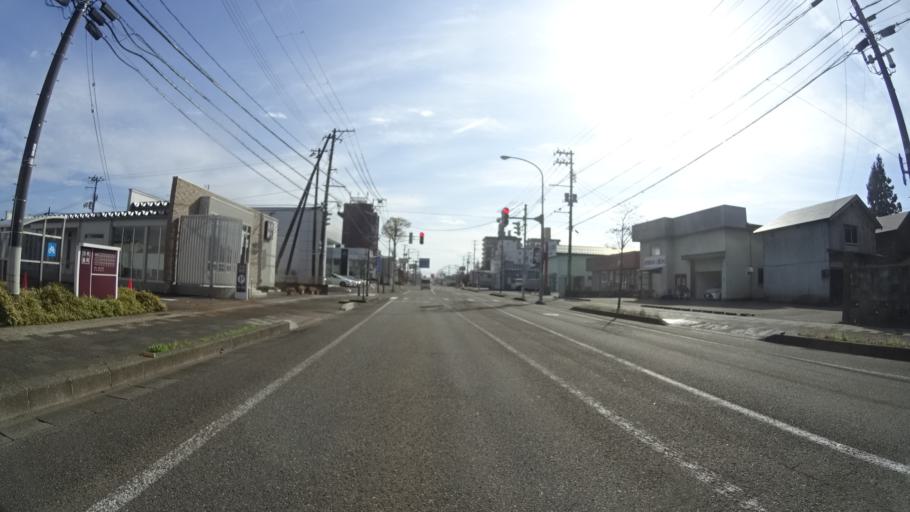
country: JP
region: Niigata
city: Joetsu
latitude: 37.1511
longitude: 138.2389
